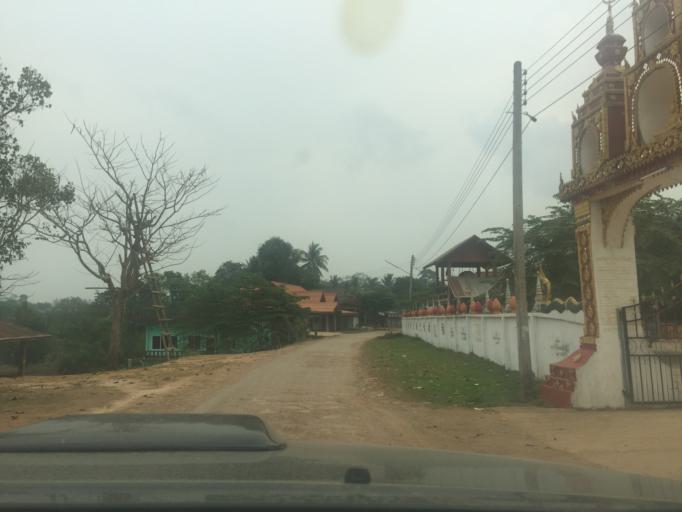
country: LA
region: Vientiane
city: Muang Sanakham
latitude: 18.4041
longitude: 101.5078
